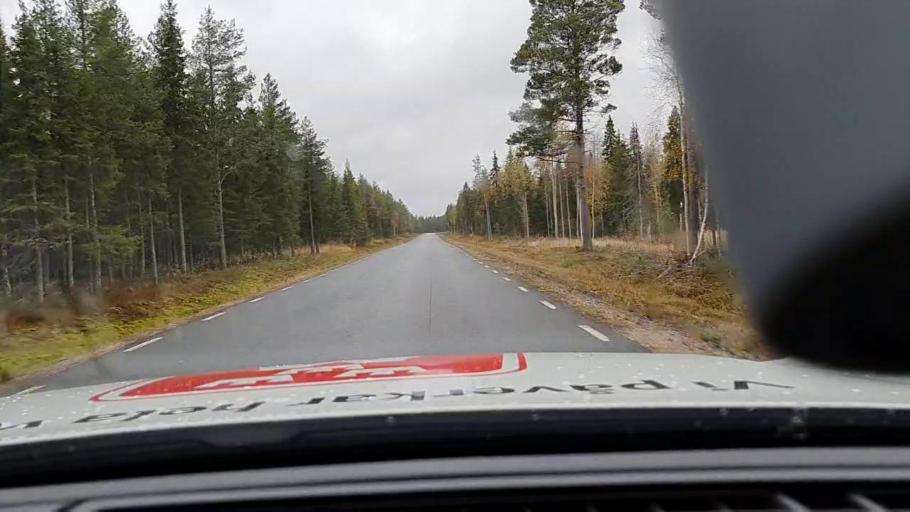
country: SE
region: Norrbotten
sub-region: Haparanda Kommun
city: Haparanda
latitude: 65.9359
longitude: 23.8104
